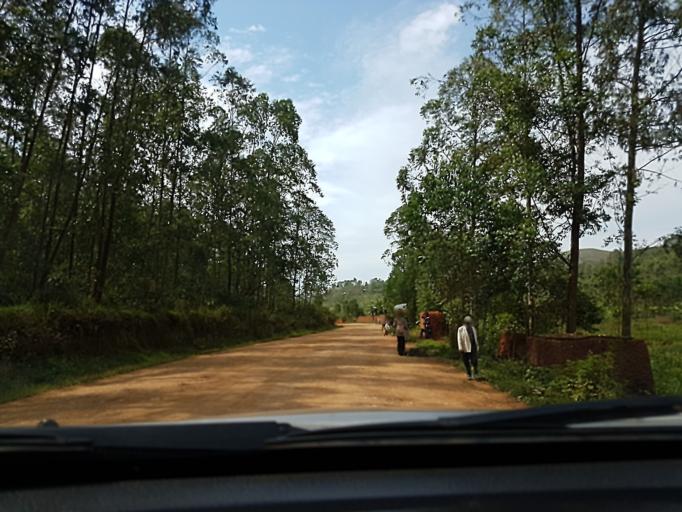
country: CD
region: South Kivu
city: Bukavu
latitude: -2.6493
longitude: 28.8737
